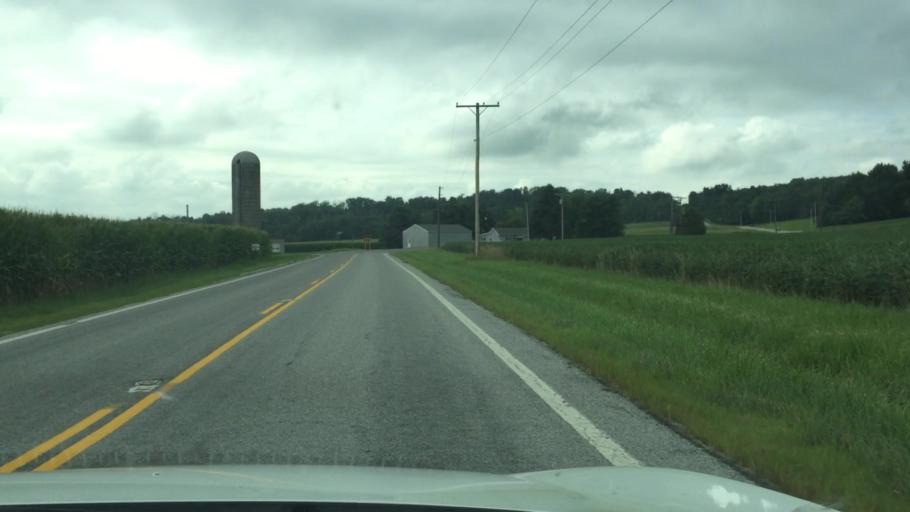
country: US
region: Ohio
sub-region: Champaign County
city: Mechanicsburg
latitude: 40.0583
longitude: -83.6163
